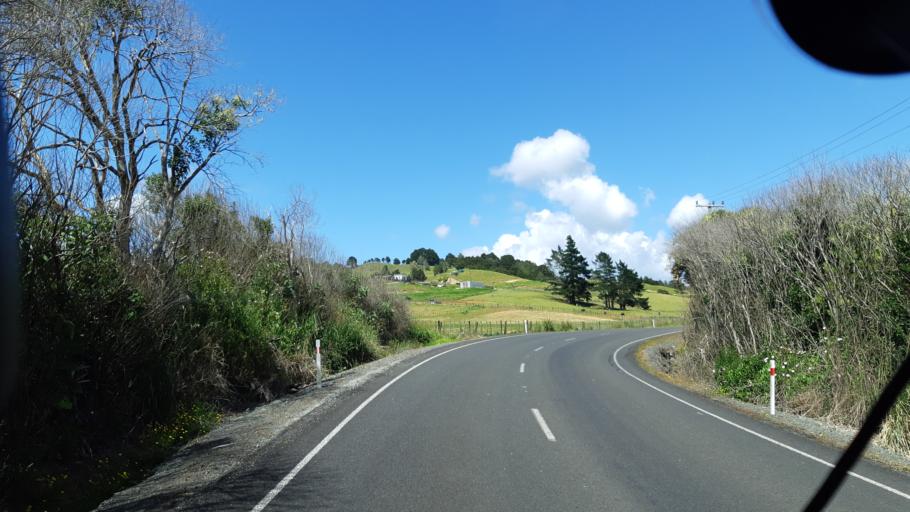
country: NZ
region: Northland
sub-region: Far North District
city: Taipa
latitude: -35.2678
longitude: 173.4966
